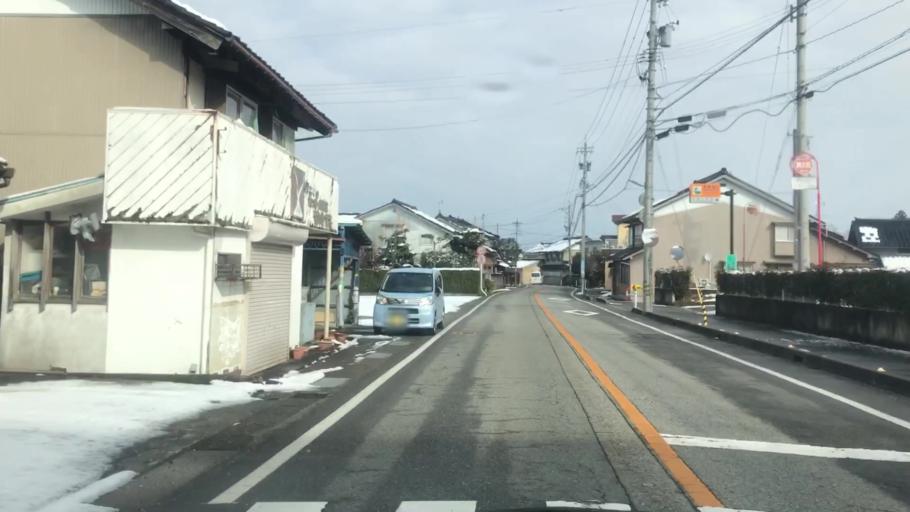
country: JP
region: Toyama
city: Toyama-shi
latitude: 36.6229
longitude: 137.2524
